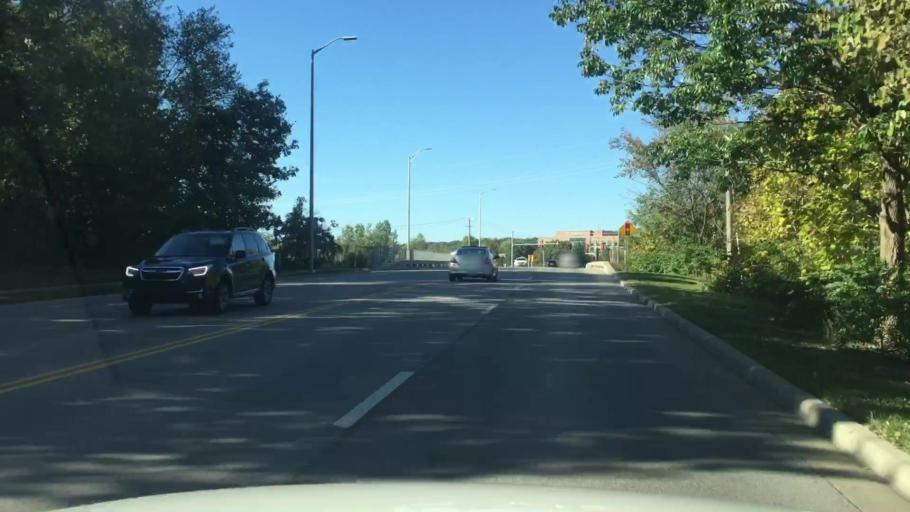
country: US
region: Kansas
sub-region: Johnson County
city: Leawood
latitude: 38.9304
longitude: -94.6291
